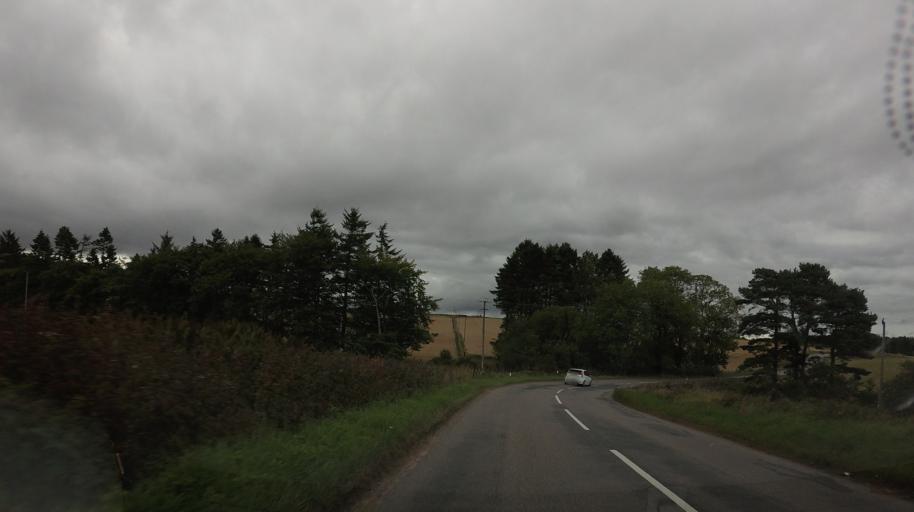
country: GB
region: Scotland
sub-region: Aberdeenshire
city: Kemnay
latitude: 57.1508
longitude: -2.4357
